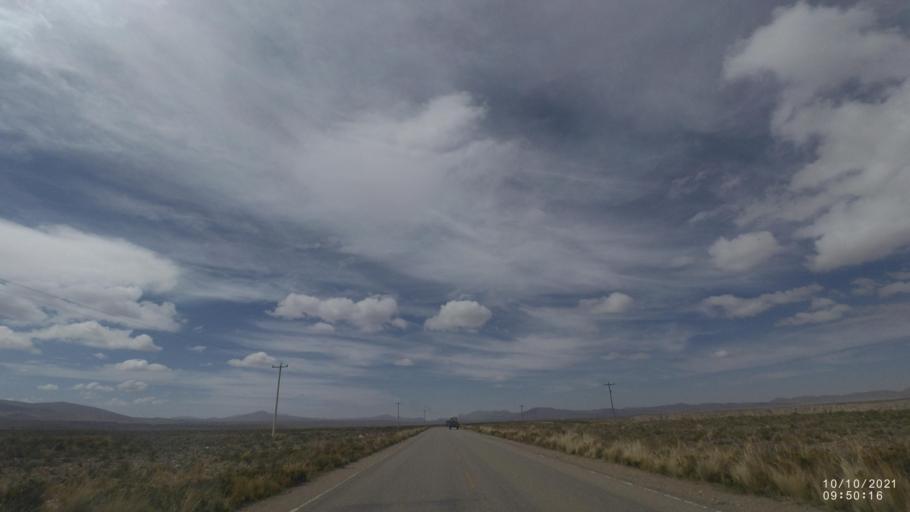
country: BO
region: La Paz
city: Colquiri
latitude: -17.2402
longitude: -67.3337
